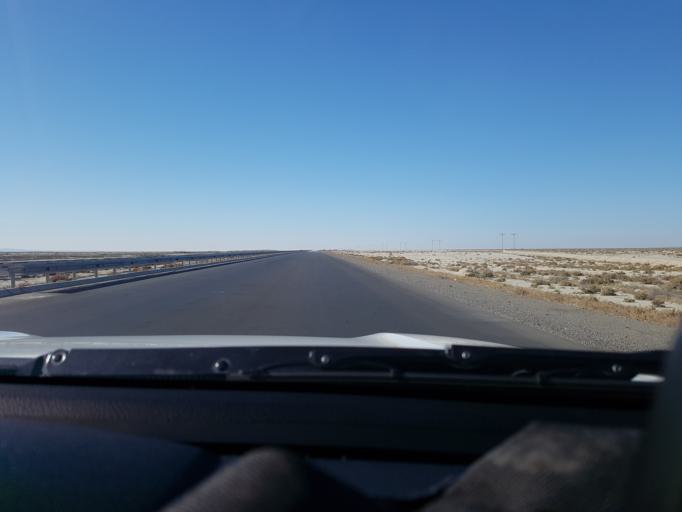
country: TM
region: Balkan
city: Gazanjyk
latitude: 39.2547
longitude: 55.1049
